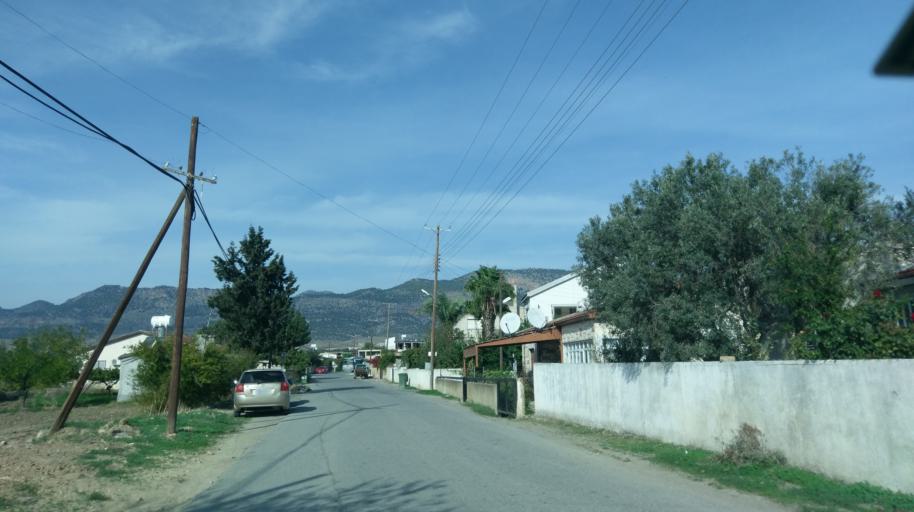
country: CY
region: Keryneia
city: Lapithos
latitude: 35.2667
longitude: 33.2243
